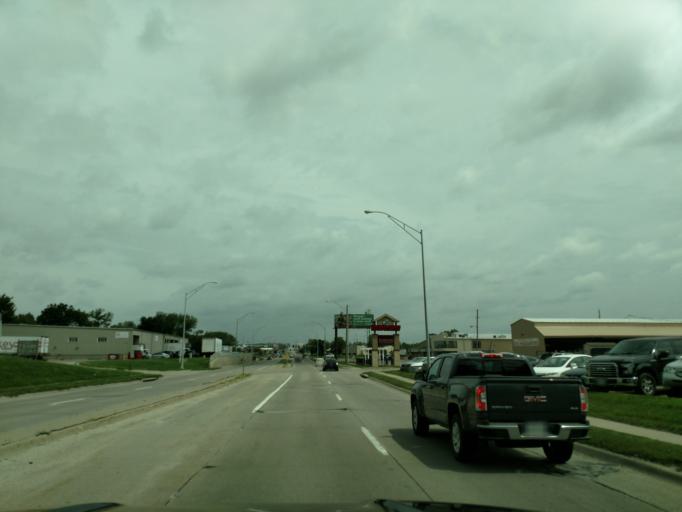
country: US
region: Nebraska
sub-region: Sarpy County
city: La Vista
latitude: 41.1995
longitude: -96.0238
